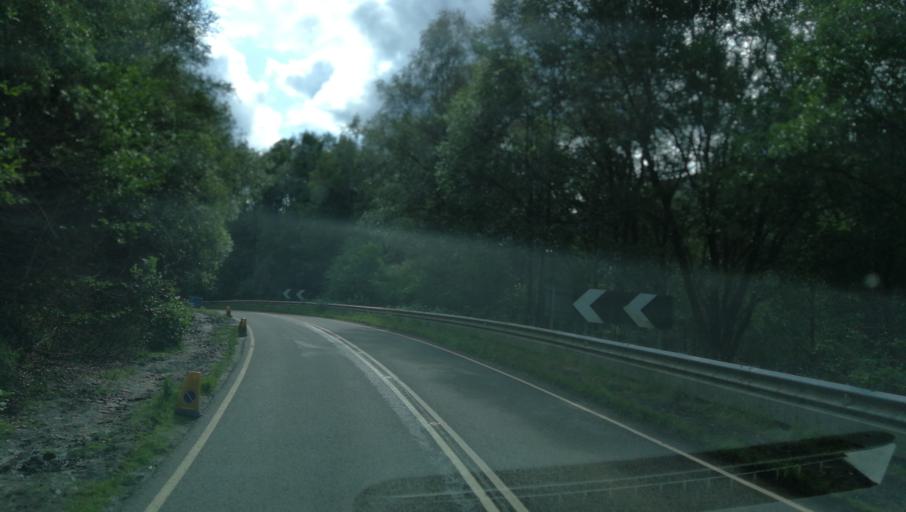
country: GB
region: Scotland
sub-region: Highland
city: Fort William
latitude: 56.8689
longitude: -5.4339
